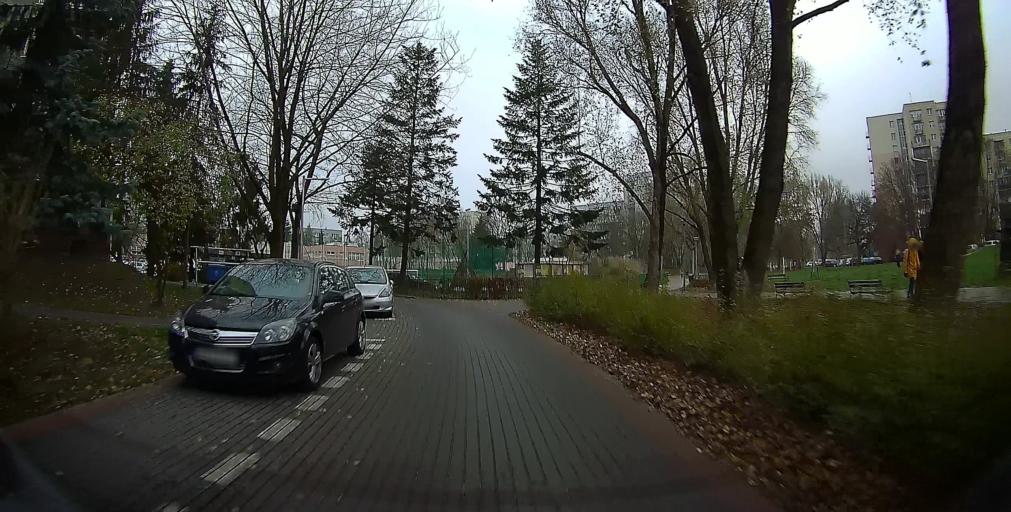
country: PL
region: Masovian Voivodeship
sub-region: Warszawa
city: Ursynow
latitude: 52.1576
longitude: 21.0265
